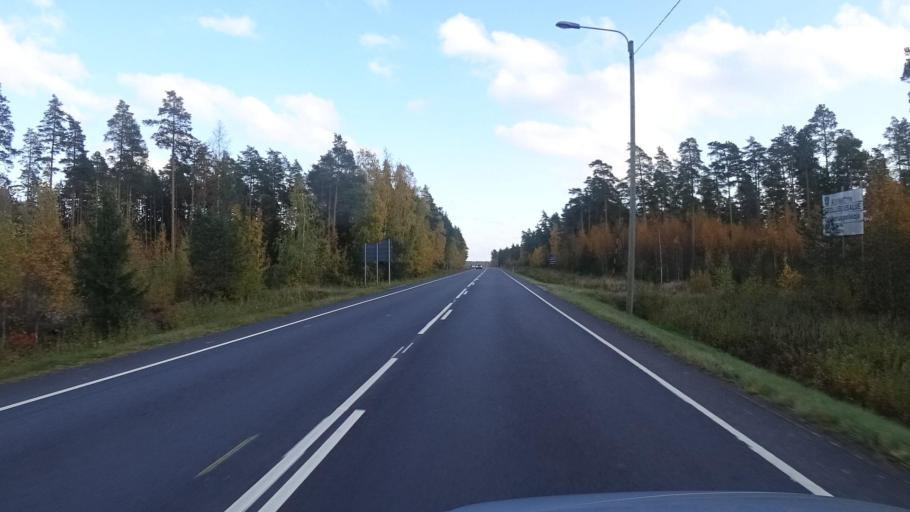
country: FI
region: Satakunta
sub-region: Rauma
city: Koeylioe
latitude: 61.0810
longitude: 22.2744
